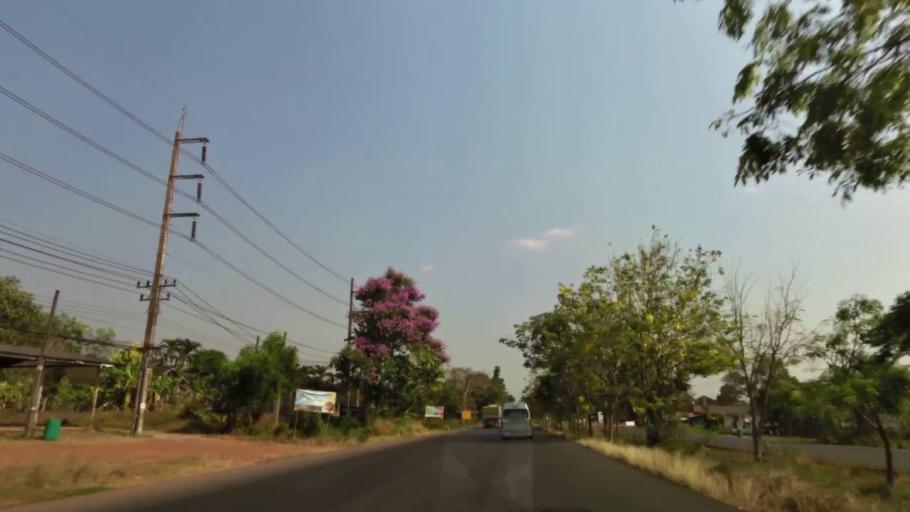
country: TH
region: Rayong
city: Wang Chan
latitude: 12.8835
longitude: 101.5585
